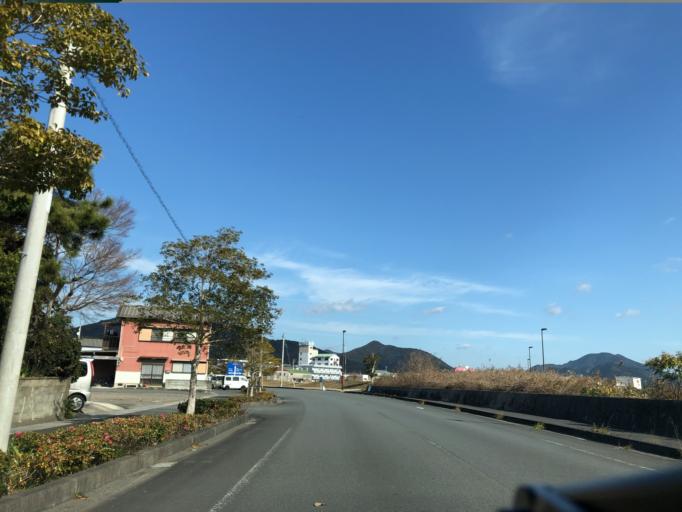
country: JP
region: Kochi
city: Sukumo
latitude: 32.9233
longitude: 132.7023
